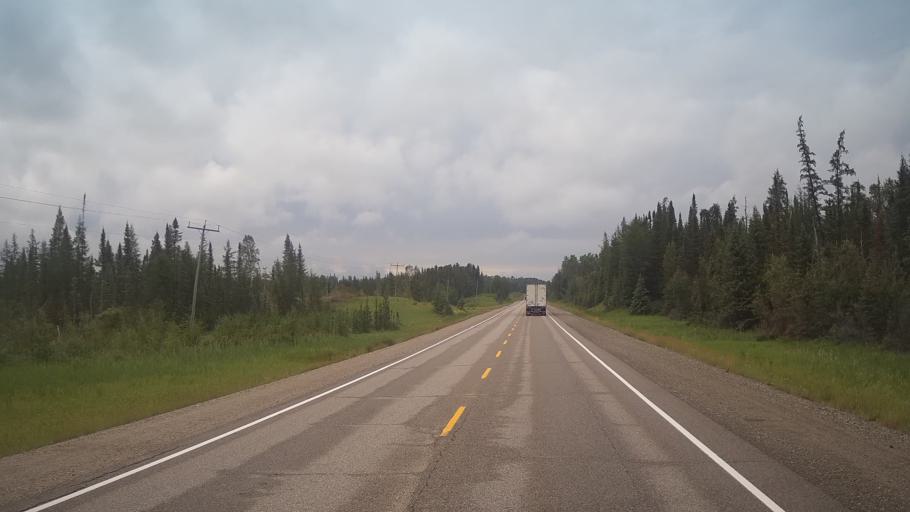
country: CA
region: Ontario
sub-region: Thunder Bay District
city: Thunder Bay
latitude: 48.7252
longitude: -89.8851
